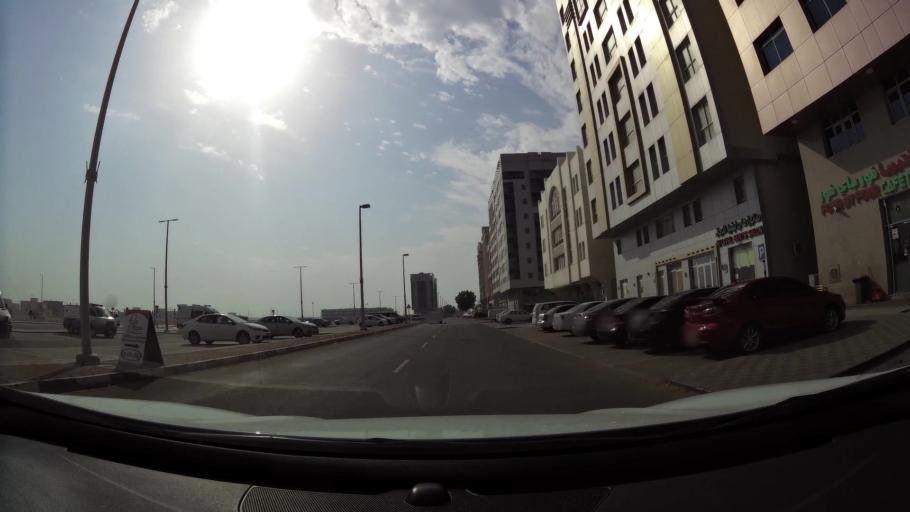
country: AE
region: Abu Dhabi
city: Abu Dhabi
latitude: 24.3179
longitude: 54.5380
